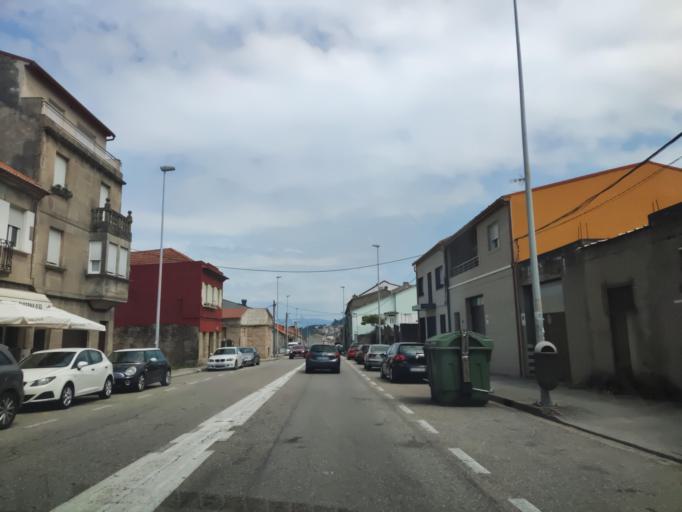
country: ES
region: Galicia
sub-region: Provincia de Pontevedra
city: Vigo
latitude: 42.2583
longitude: -8.6805
